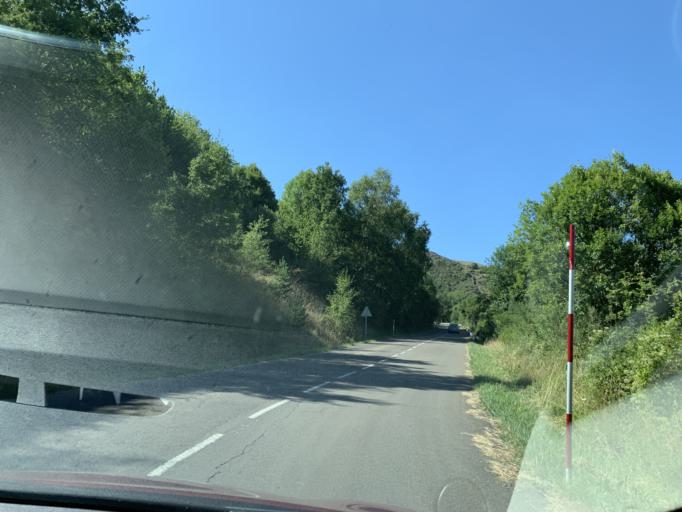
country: ES
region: Aragon
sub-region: Provincia de Huesca
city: Hoz de Jaca
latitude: 42.7022
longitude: -0.3215
